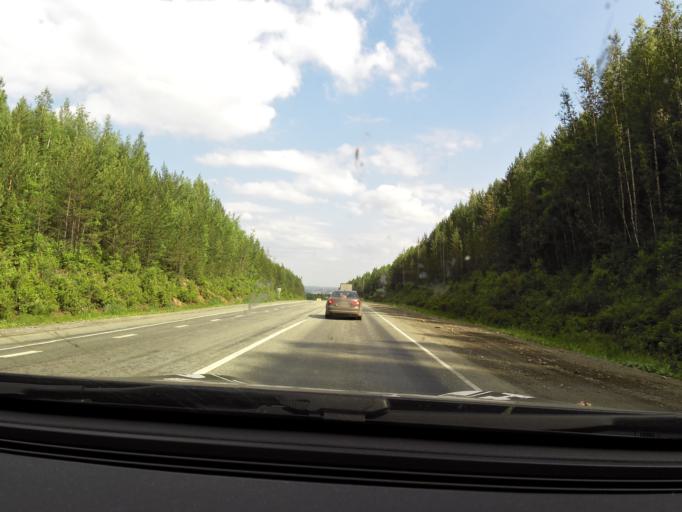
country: RU
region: Sverdlovsk
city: Revda
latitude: 56.8345
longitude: 59.8371
